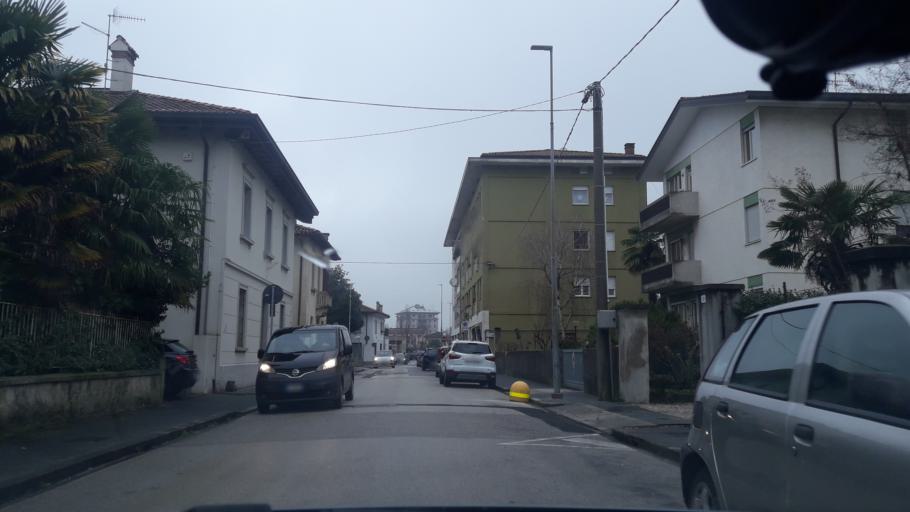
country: IT
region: Friuli Venezia Giulia
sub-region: Provincia di Udine
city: Udine
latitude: 46.0684
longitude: 13.2484
